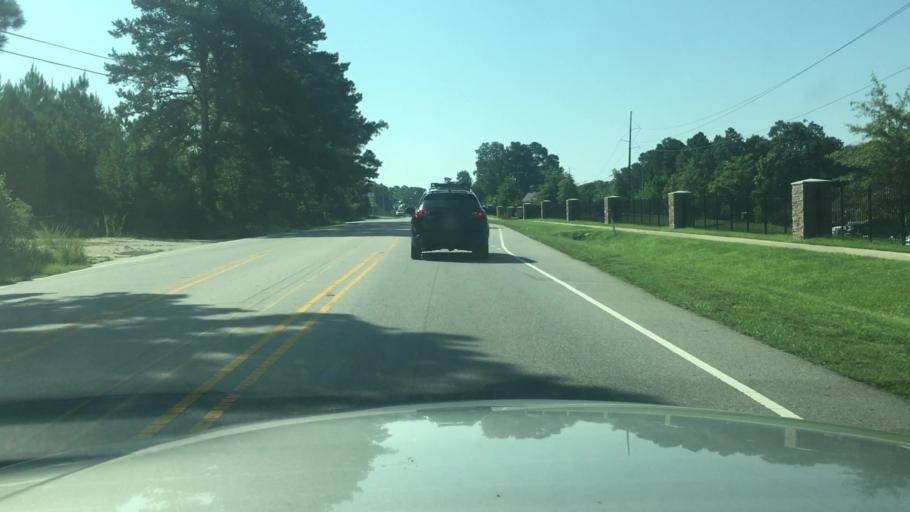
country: US
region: North Carolina
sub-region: Cumberland County
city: Fayetteville
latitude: 35.1244
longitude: -78.8876
